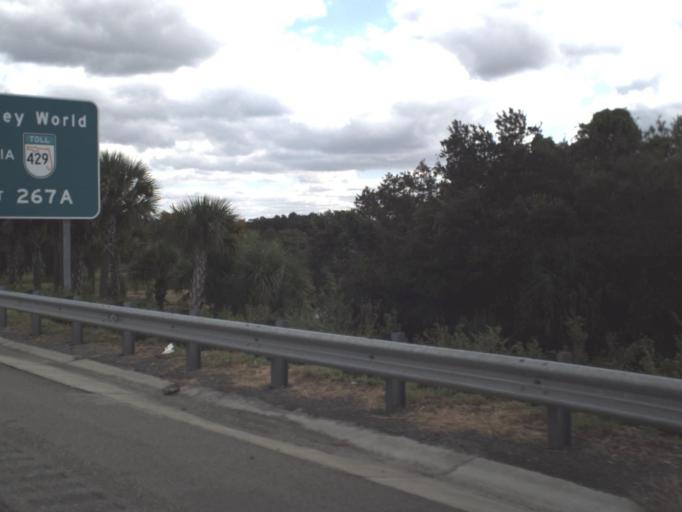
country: US
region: Florida
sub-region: Orange County
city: Oakland
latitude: 28.5450
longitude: -81.6086
